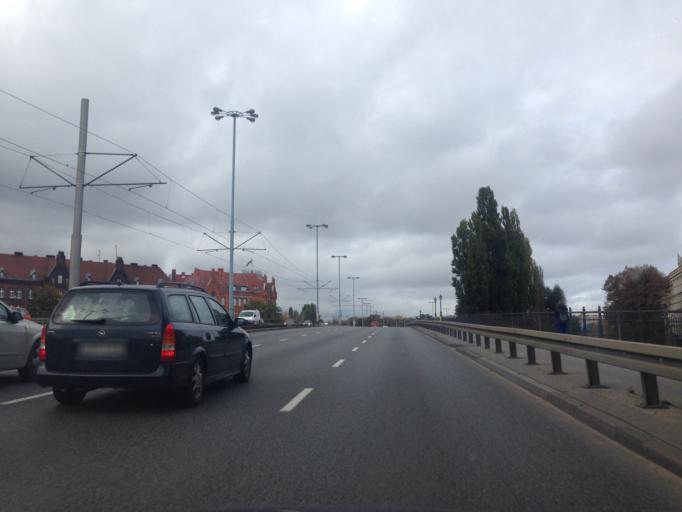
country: PL
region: Pomeranian Voivodeship
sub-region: Gdansk
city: Gdansk
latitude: 54.3587
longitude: 18.6456
